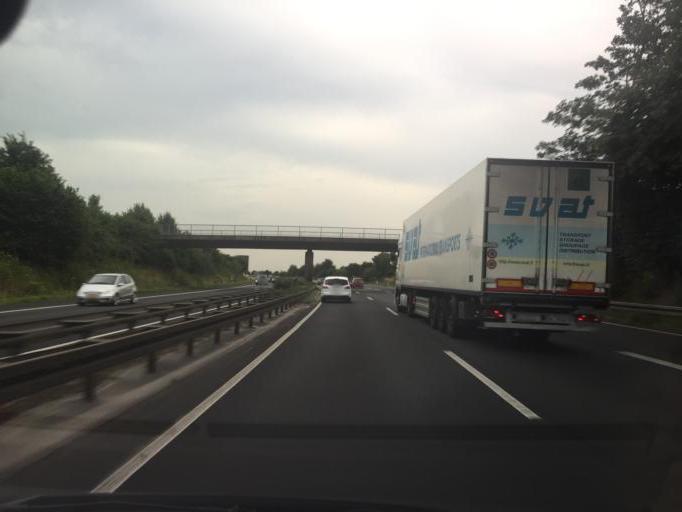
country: DE
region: North Rhine-Westphalia
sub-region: Regierungsbezirk Dusseldorf
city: Nettetal
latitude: 51.3107
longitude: 6.2263
